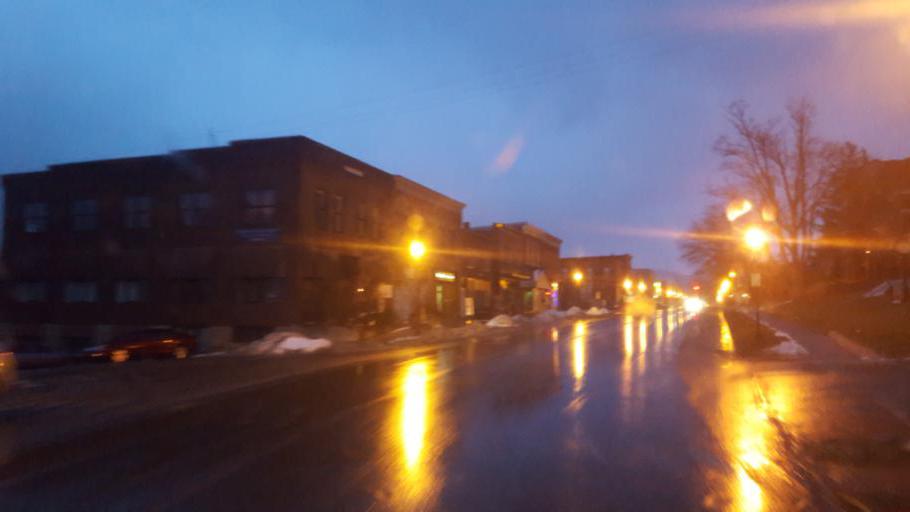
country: US
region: Pennsylvania
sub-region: McKean County
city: Smethport
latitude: 41.8095
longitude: -78.4428
